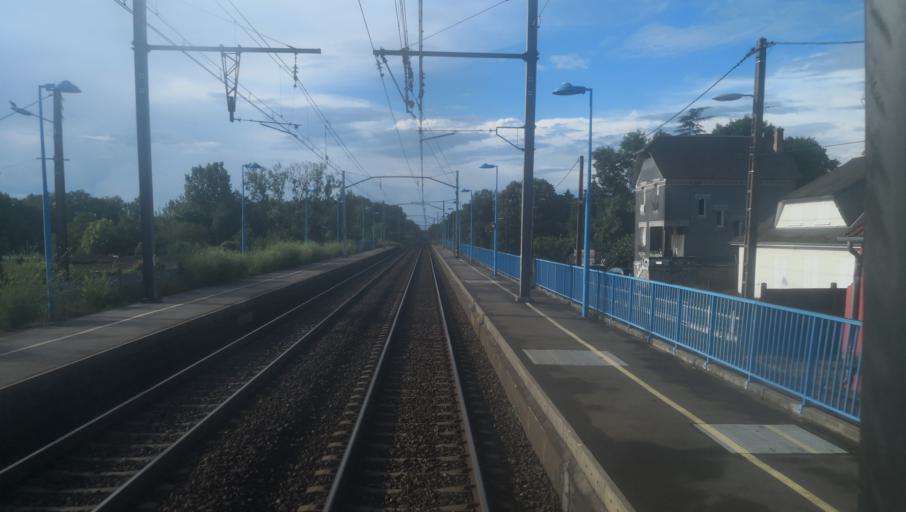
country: FR
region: Centre
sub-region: Departement du Loir-et-Cher
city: Salbris
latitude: 47.4257
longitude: 2.0475
